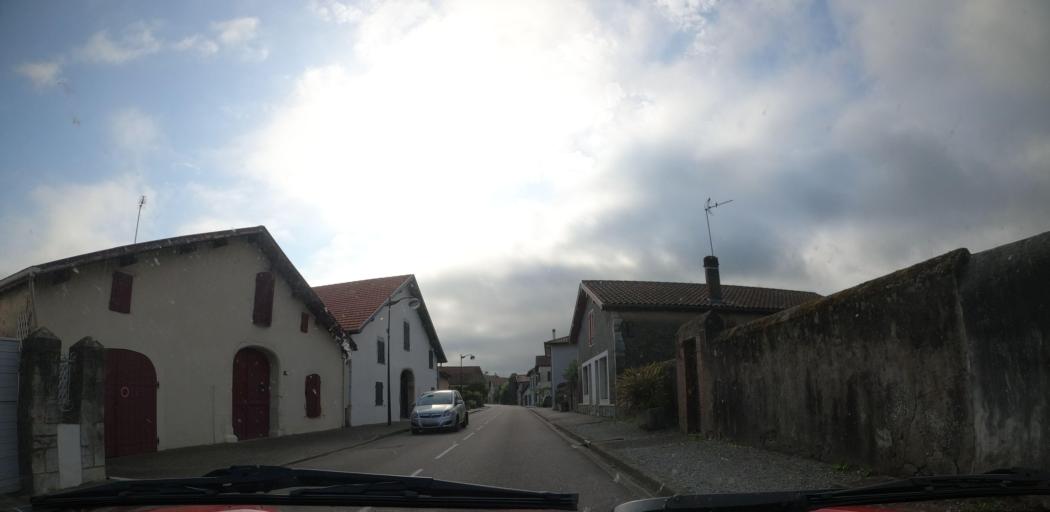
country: FR
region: Aquitaine
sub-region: Departement des Landes
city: Peyrehorade
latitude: 43.5302
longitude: -1.0575
